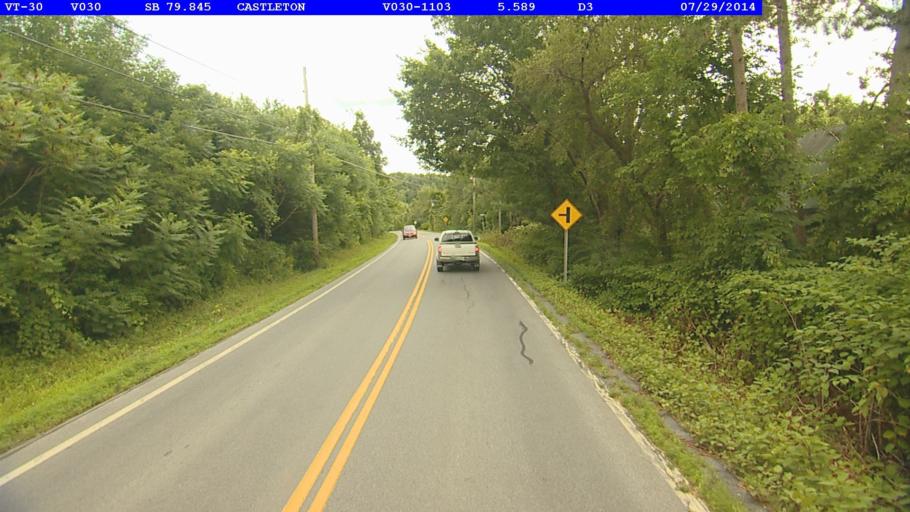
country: US
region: Vermont
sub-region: Rutland County
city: Castleton
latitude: 43.6651
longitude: -73.1914
